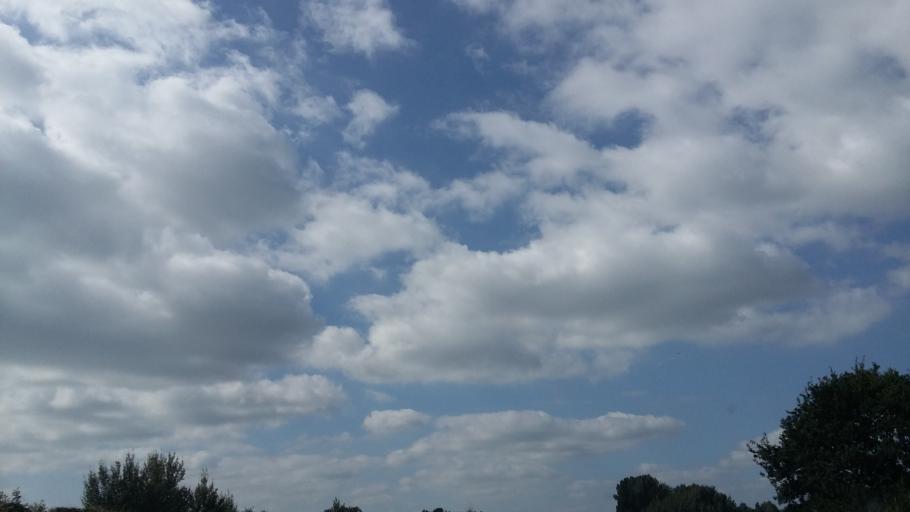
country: DE
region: Lower Saxony
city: Ritterhude
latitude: 53.1386
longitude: 8.7445
